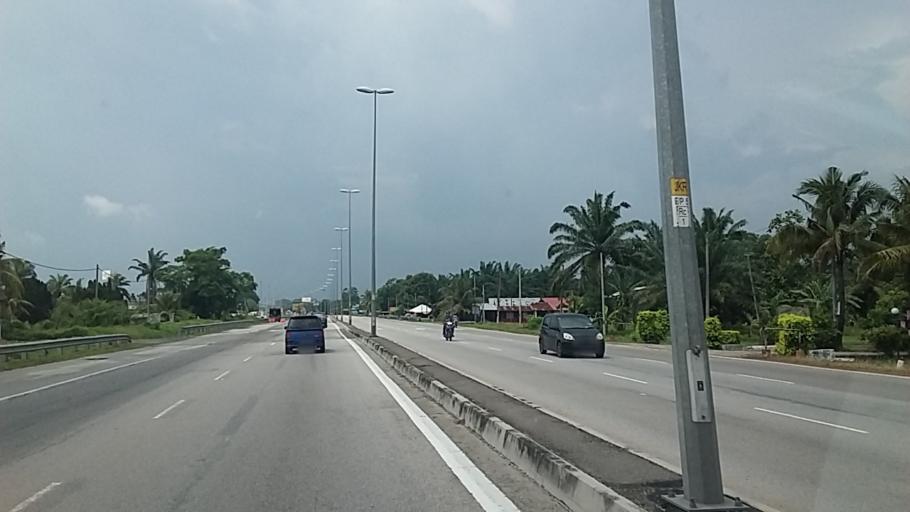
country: MY
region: Johor
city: Parit Raja
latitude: 1.8535
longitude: 103.0900
